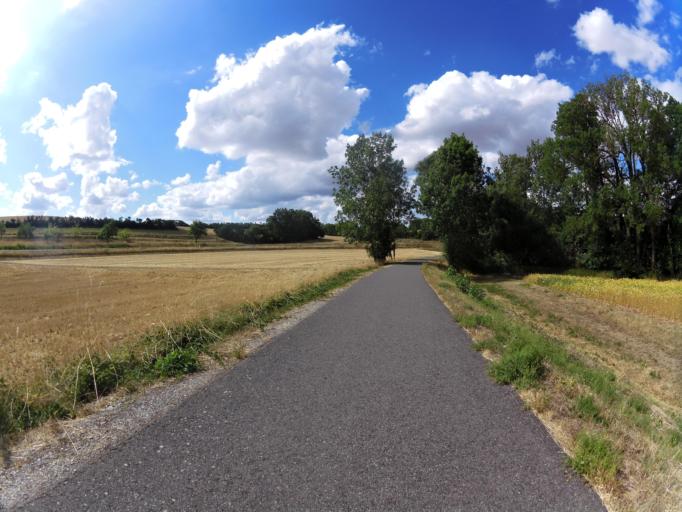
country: DE
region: Bavaria
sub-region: Regierungsbezirk Unterfranken
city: Gaukonigshofen
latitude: 49.6379
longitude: 9.9980
